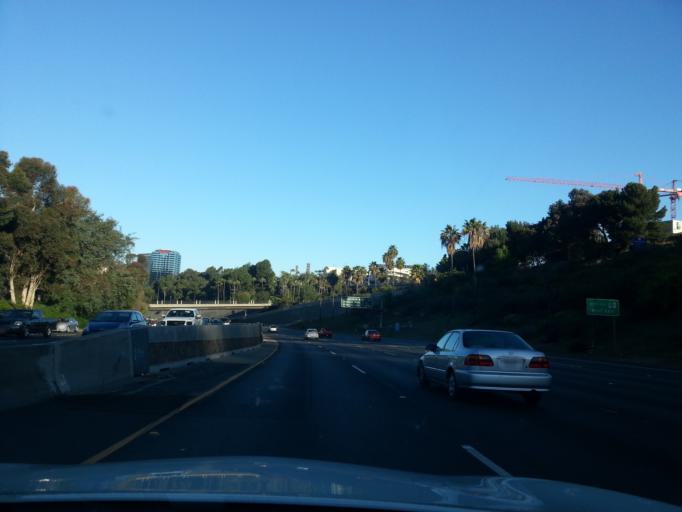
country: US
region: California
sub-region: Los Angeles County
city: Universal City
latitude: 34.1316
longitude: -118.3499
